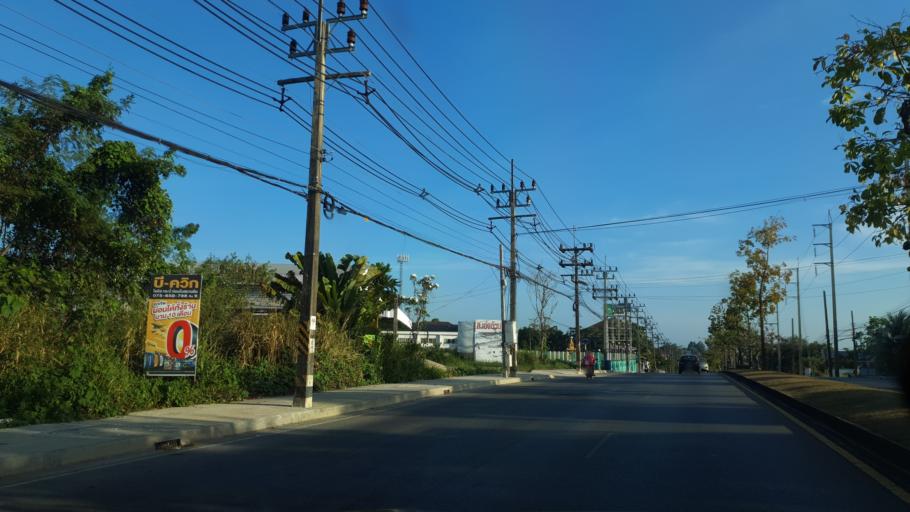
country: TH
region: Krabi
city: Krabi
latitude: 8.0938
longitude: 98.8900
